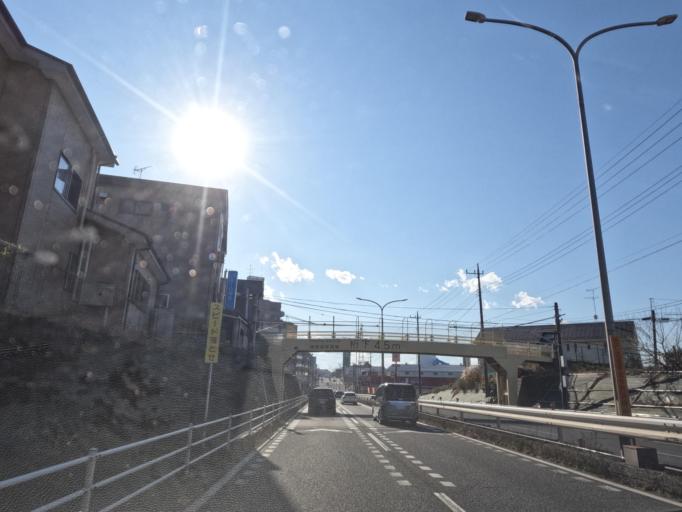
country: JP
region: Saitama
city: Wako
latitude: 35.7865
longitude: 139.6251
